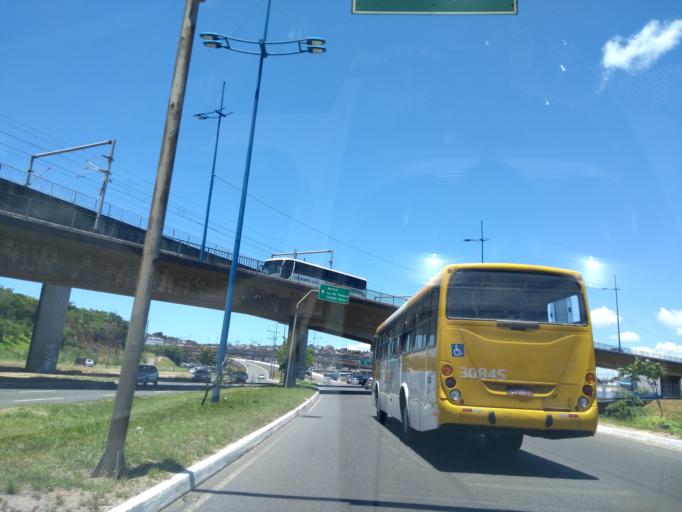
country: BR
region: Bahia
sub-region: Salvador
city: Salvador
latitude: -12.9727
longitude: -38.4773
